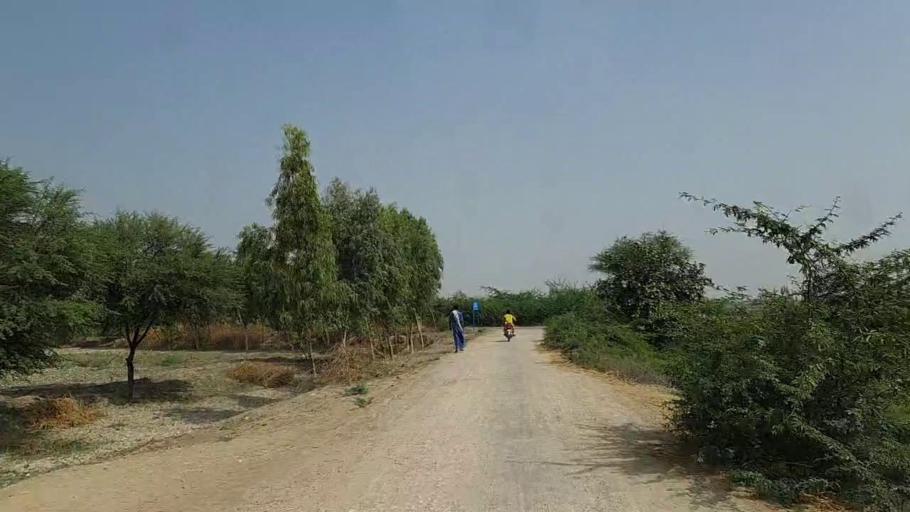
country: PK
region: Sindh
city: Naukot
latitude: 24.7778
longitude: 69.3562
